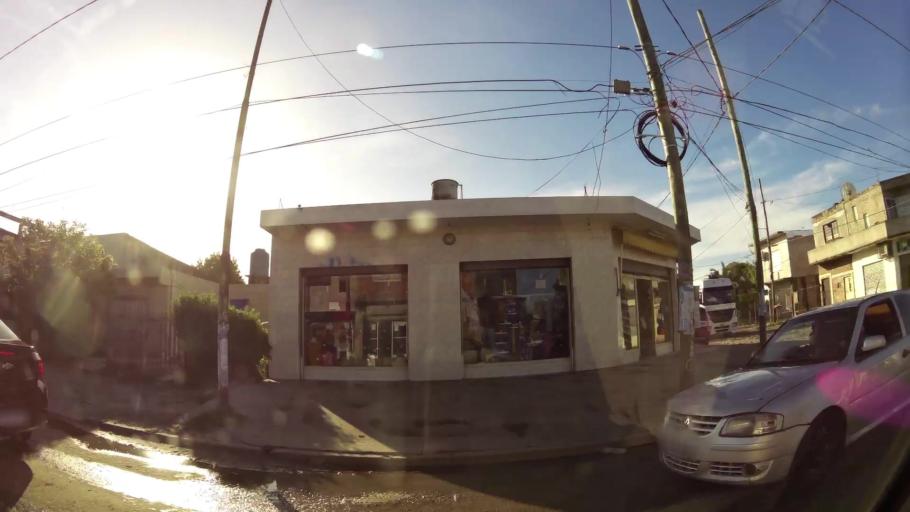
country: AR
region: Buenos Aires
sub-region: Partido de Quilmes
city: Quilmes
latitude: -34.8201
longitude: -58.2082
